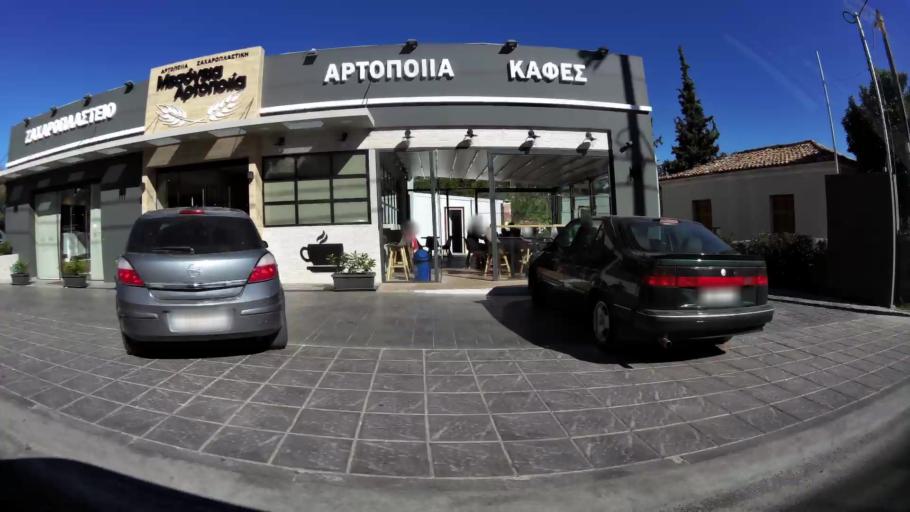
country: GR
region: Attica
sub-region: Nomarchia Anatolikis Attikis
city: Paiania
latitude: 37.9602
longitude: 23.8561
